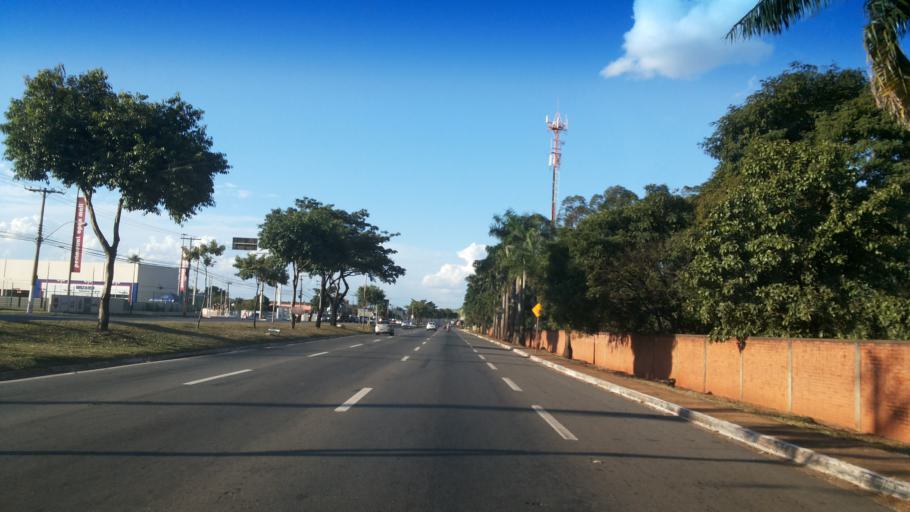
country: BR
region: Goias
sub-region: Goiania
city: Goiania
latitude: -16.6451
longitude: -49.3077
